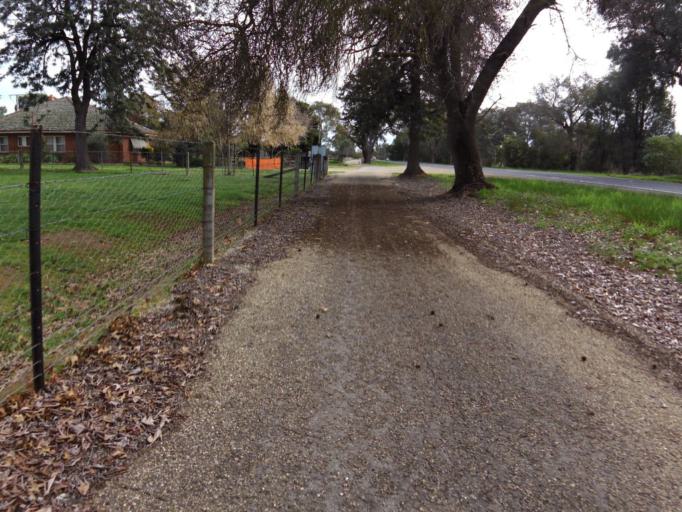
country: AU
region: Victoria
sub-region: Wangaratta
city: Wangaratta
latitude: -36.4088
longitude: 146.3508
